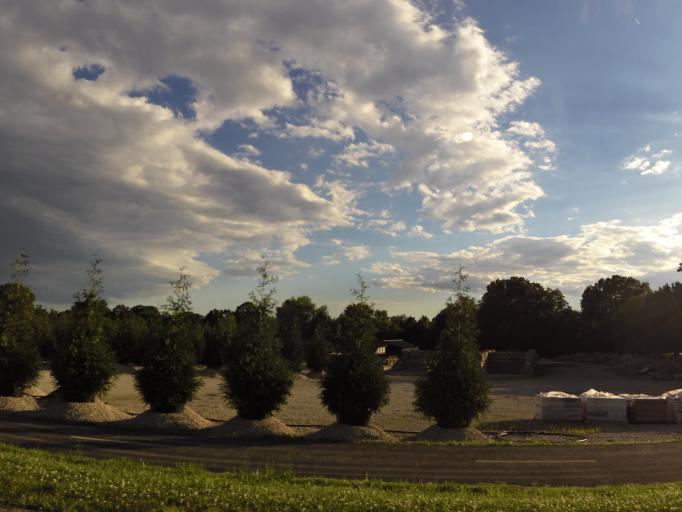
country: US
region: Missouri
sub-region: Saint Louis County
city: Wildwood
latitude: 38.5973
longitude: -90.6408
